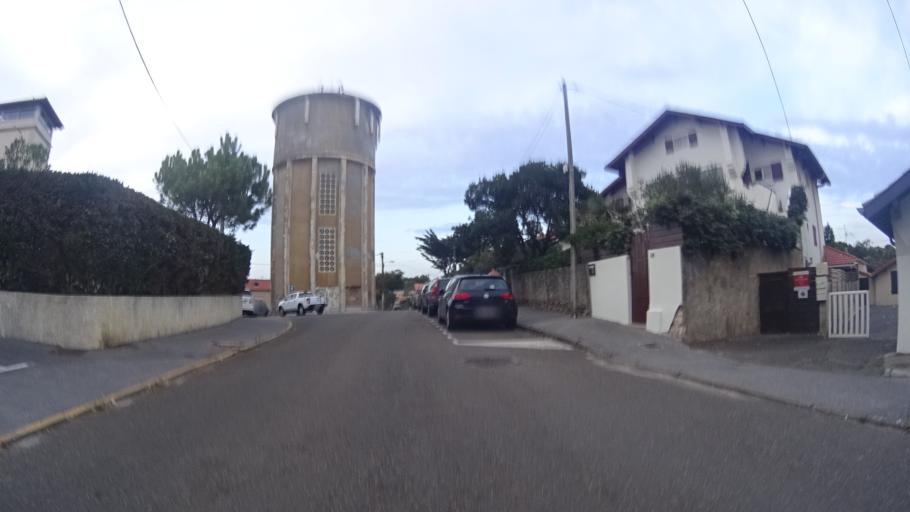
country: FR
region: Aquitaine
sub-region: Departement des Landes
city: Capbreton
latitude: 43.6501
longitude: -1.4431
